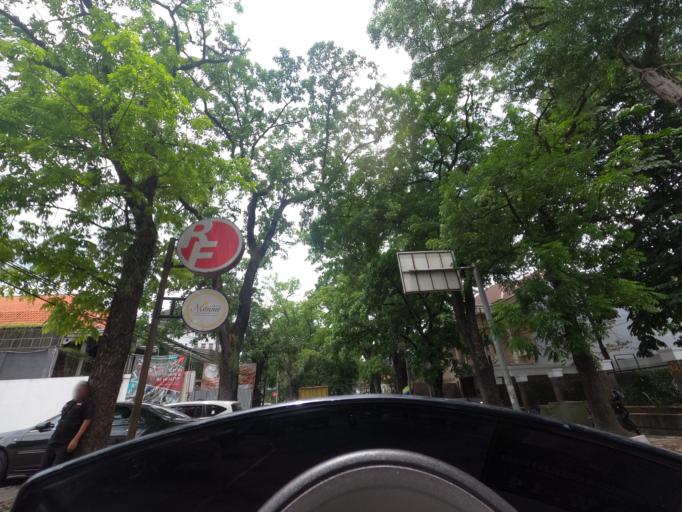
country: ID
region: West Java
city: Bandung
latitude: -6.9073
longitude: 107.6236
